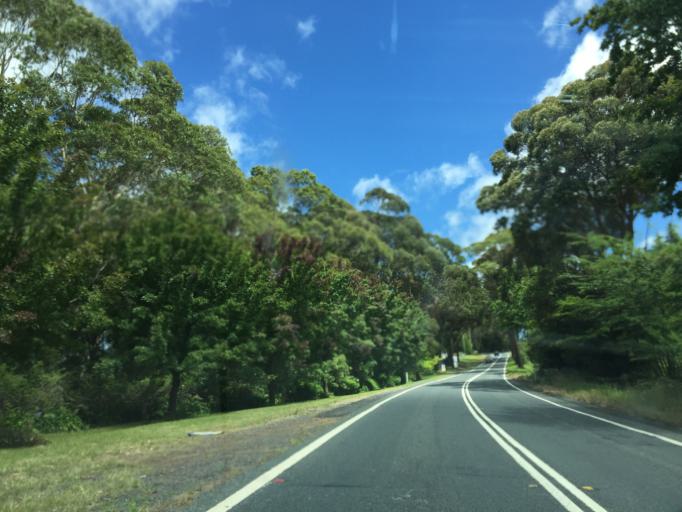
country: AU
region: New South Wales
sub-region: Blue Mountains Municipality
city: Hazelbrook
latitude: -33.5177
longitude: 150.4816
